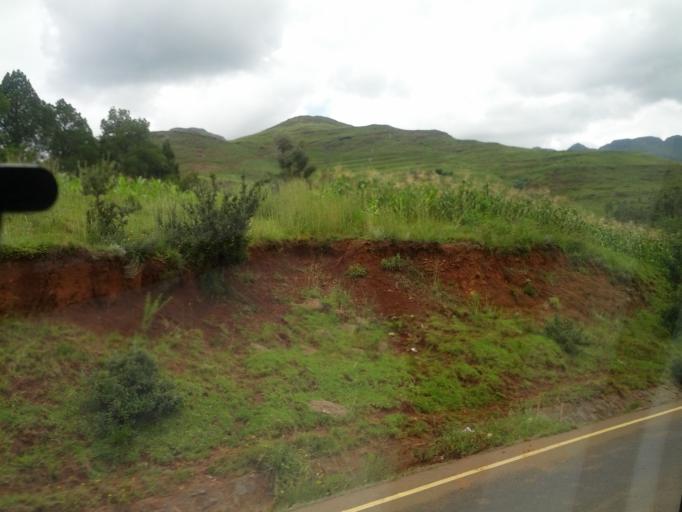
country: LS
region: Butha-Buthe
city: Butha-Buthe
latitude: -29.0342
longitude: 28.2846
